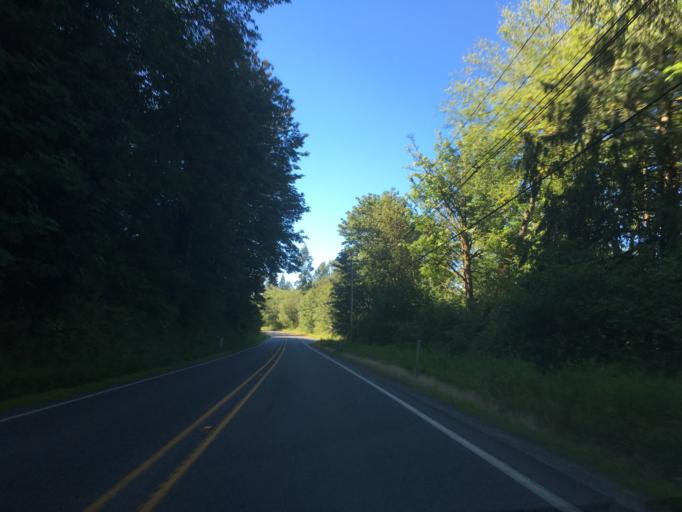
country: US
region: Washington
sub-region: Skagit County
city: Big Lake
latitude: 48.4273
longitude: -122.2589
